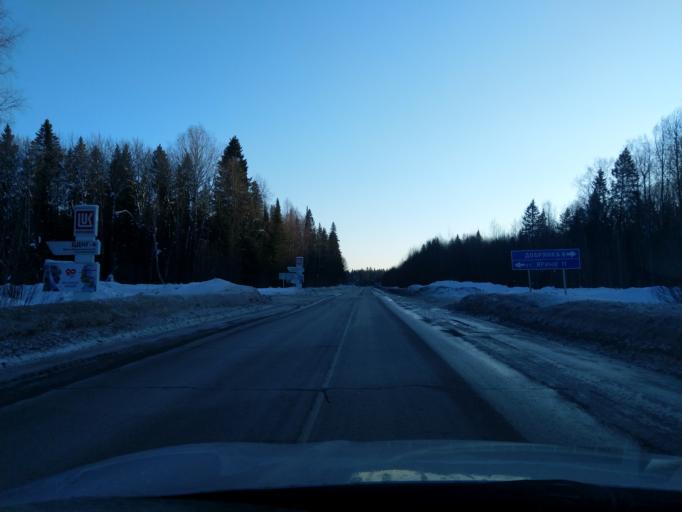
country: RU
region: Perm
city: Dobryanka
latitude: 58.4481
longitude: 56.5435
